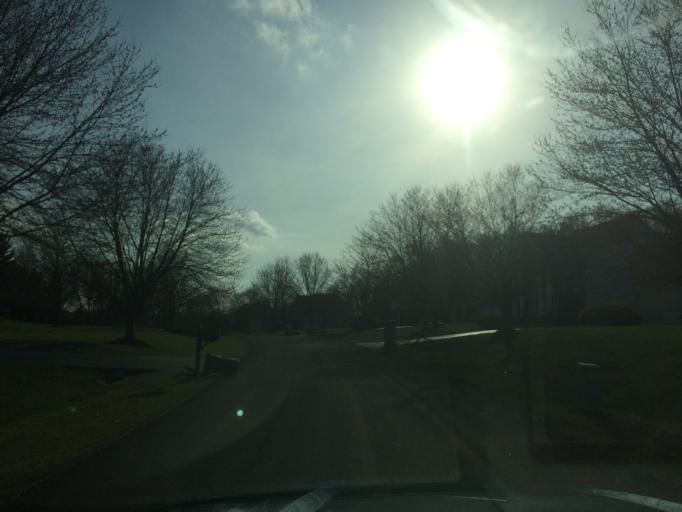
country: US
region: Maryland
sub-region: Carroll County
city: Sykesville
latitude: 39.2860
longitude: -76.9742
